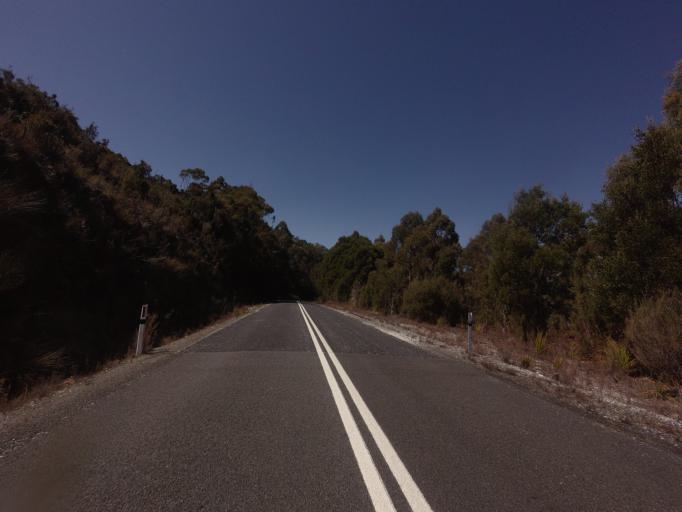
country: AU
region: Tasmania
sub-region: West Coast
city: Queenstown
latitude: -42.7962
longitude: 146.0780
